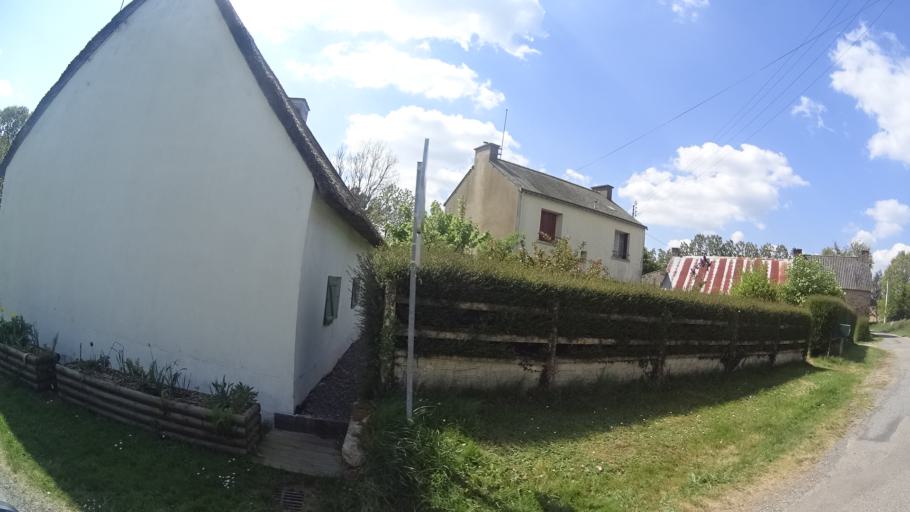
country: FR
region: Brittany
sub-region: Departement du Morbihan
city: Beganne
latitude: 47.5919
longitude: -2.2389
